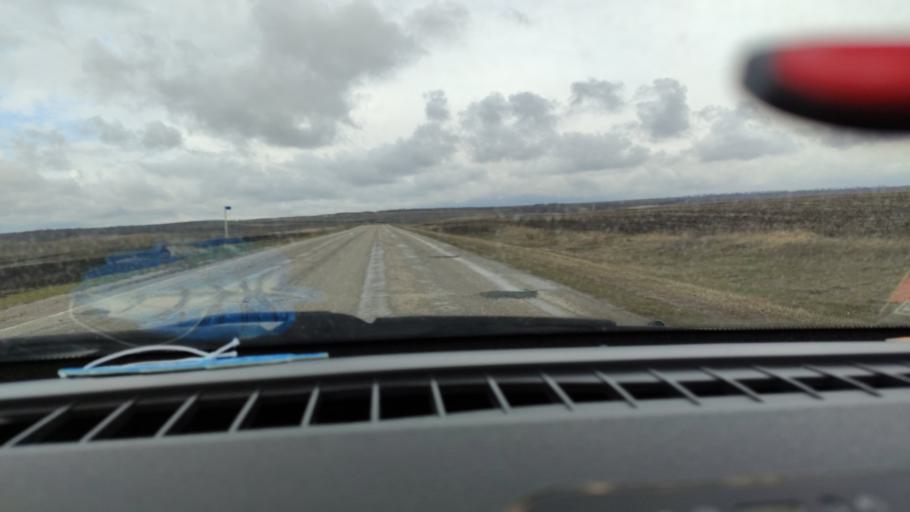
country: RU
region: Tatarstan
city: Nurlat
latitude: 54.3652
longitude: 50.6956
